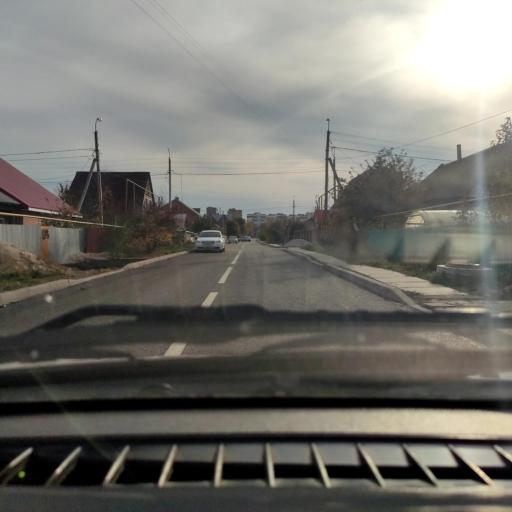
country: RU
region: Samara
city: Tol'yatti
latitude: 53.5295
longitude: 49.4216
